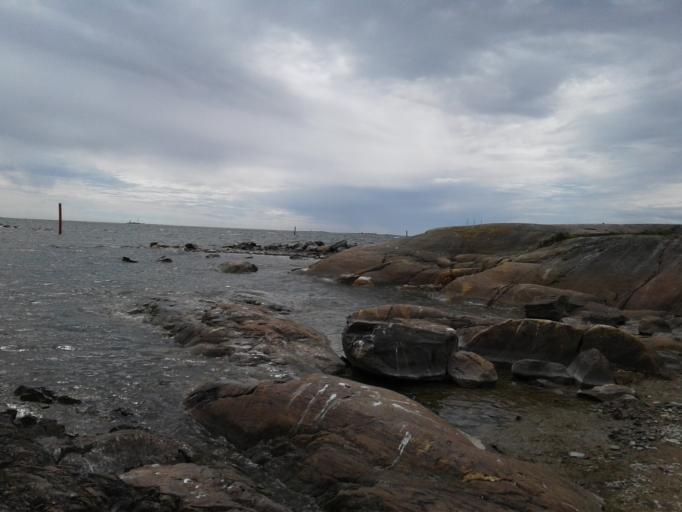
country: FI
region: Uusimaa
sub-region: Helsinki
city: Helsinki
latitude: 60.1462
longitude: 24.9774
